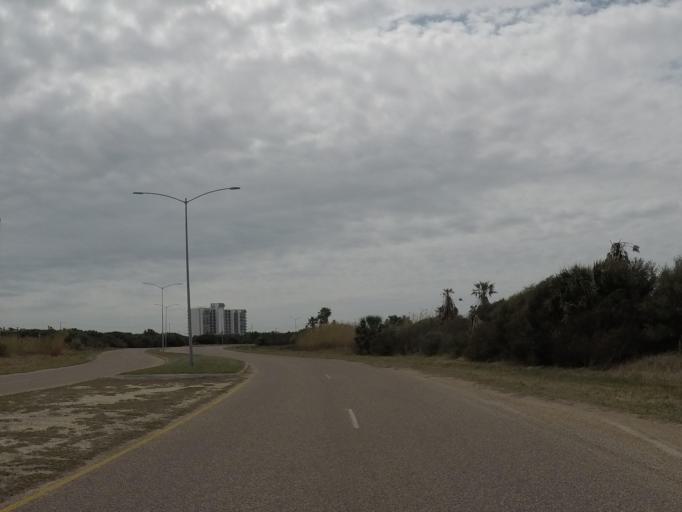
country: US
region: Texas
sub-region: Galveston County
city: Galveston
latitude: 29.3193
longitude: -94.7557
